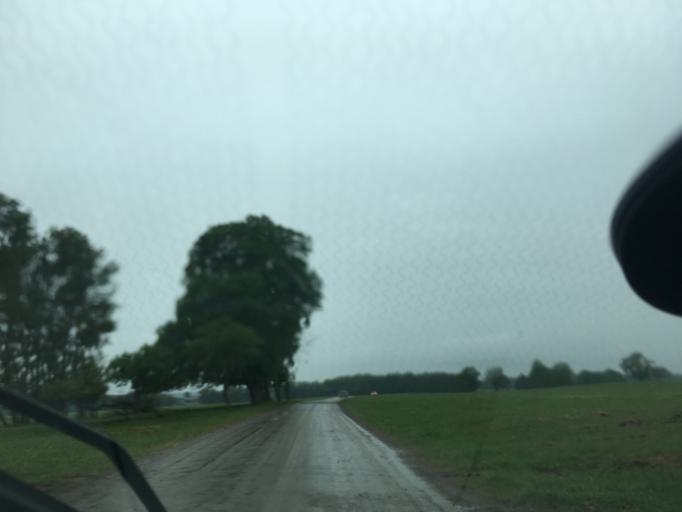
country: SE
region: Skane
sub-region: Lunds Kommun
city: Veberod
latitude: 55.6640
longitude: 13.4846
